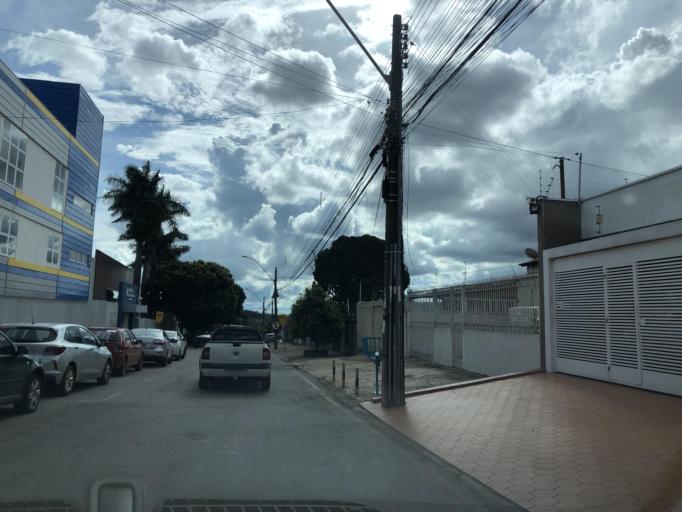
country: BR
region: Federal District
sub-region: Brasilia
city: Brasilia
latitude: -15.8373
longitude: -48.0578
